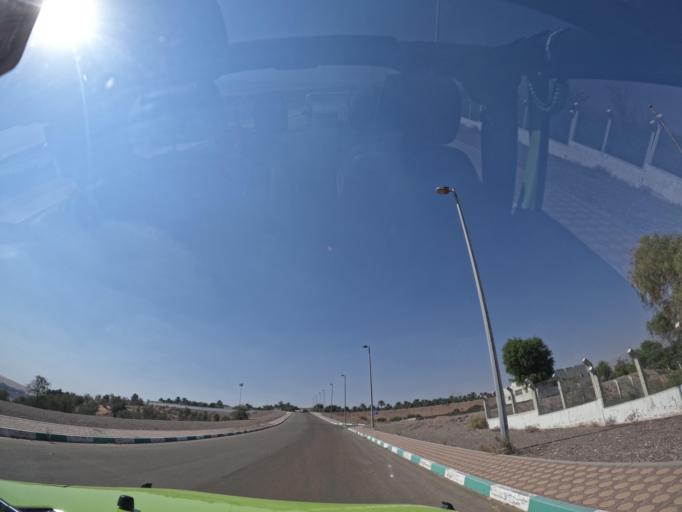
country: AE
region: Ash Shariqah
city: Adh Dhayd
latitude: 24.7858
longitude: 55.8126
